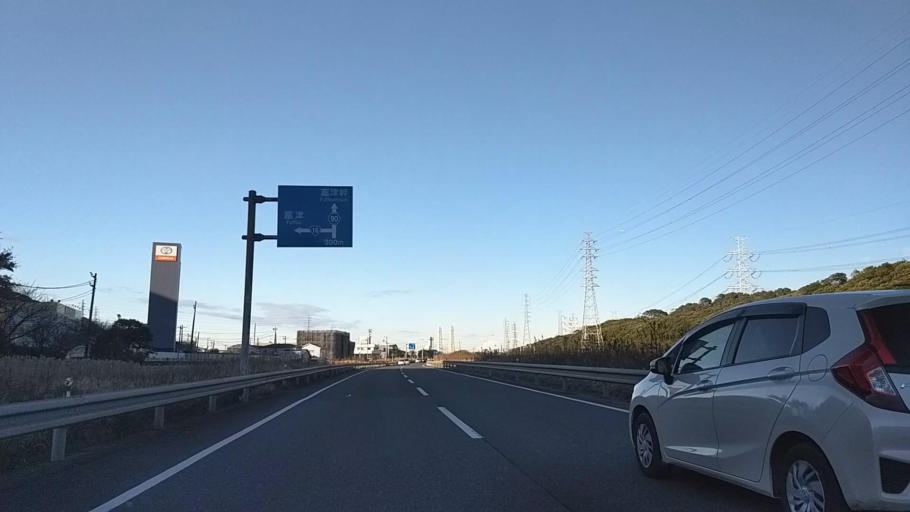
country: JP
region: Chiba
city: Kimitsu
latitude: 35.3448
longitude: 139.8797
